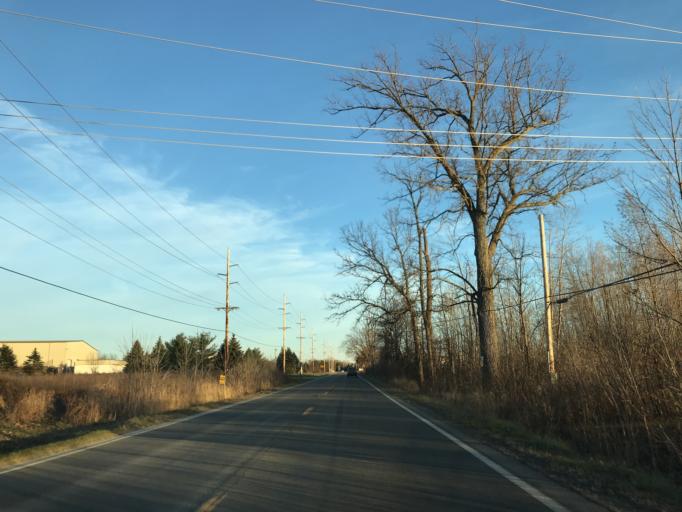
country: US
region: Michigan
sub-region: Livingston County
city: Whitmore Lake
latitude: 42.3781
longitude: -83.7432
